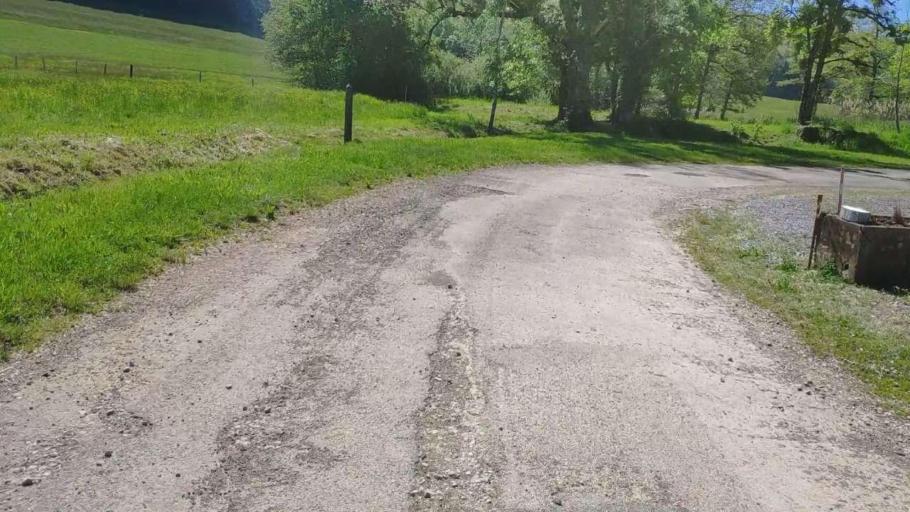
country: FR
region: Franche-Comte
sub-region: Departement du Jura
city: Poligny
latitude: 46.7193
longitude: 5.7430
